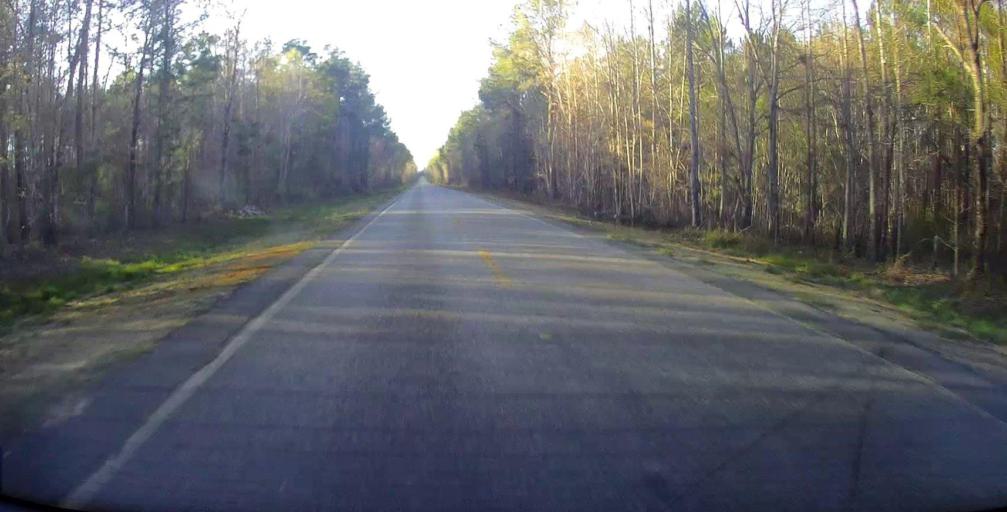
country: US
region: Georgia
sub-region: Wilcox County
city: Abbeville
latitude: 32.0924
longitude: -83.2970
